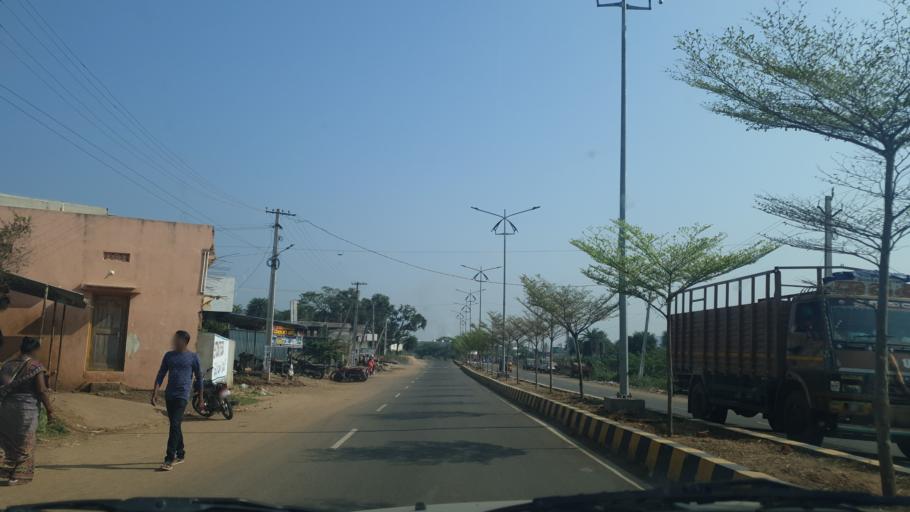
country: IN
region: Andhra Pradesh
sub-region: Srikakulam
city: Tekkali
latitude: 18.6124
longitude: 84.2348
